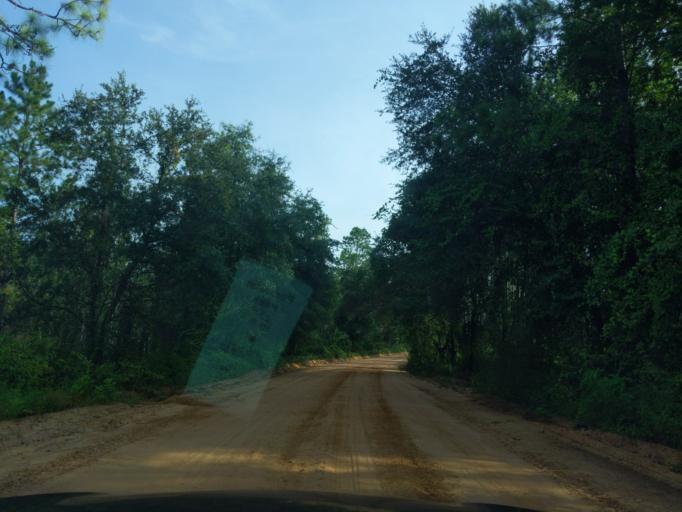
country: US
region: Florida
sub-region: Gadsden County
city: Midway
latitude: 30.3959
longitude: -84.4091
